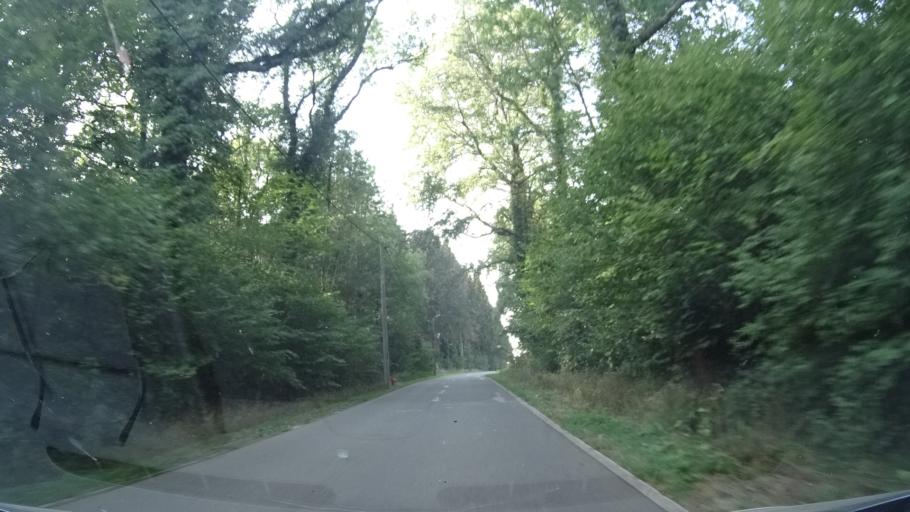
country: BE
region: Wallonia
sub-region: Province du Hainaut
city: Froidchapelle
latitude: 50.2160
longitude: 4.3436
